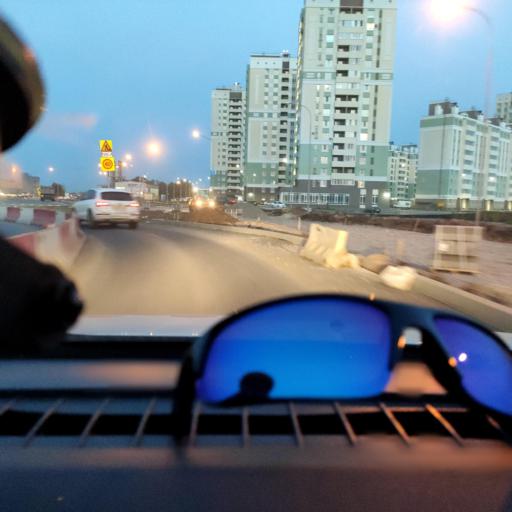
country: RU
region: Samara
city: Samara
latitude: 53.1071
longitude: 50.1359
